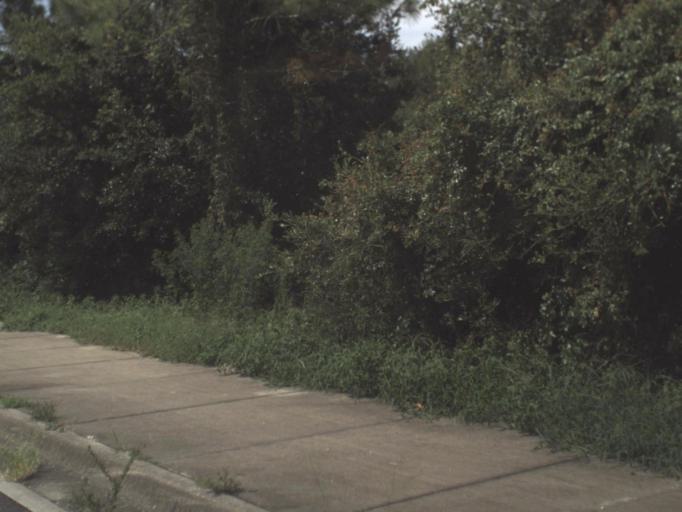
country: US
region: Florida
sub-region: Citrus County
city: Inverness Highlands South
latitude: 28.8047
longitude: -82.3112
